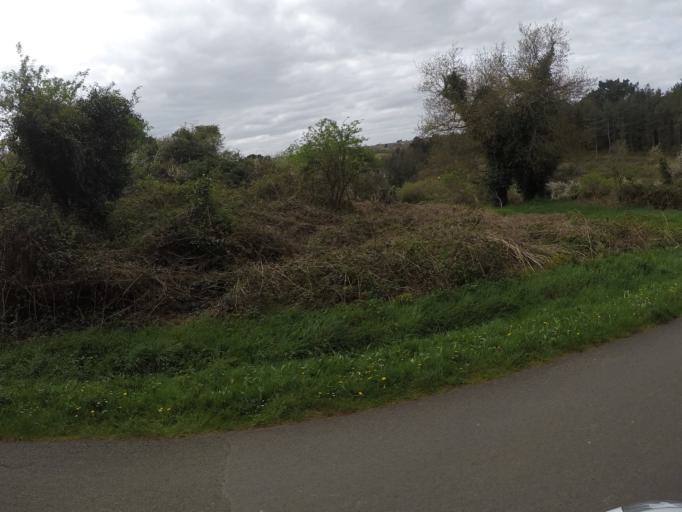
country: FR
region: Brittany
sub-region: Departement des Cotes-d'Armor
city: Plouezec
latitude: 48.7296
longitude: -2.9455
